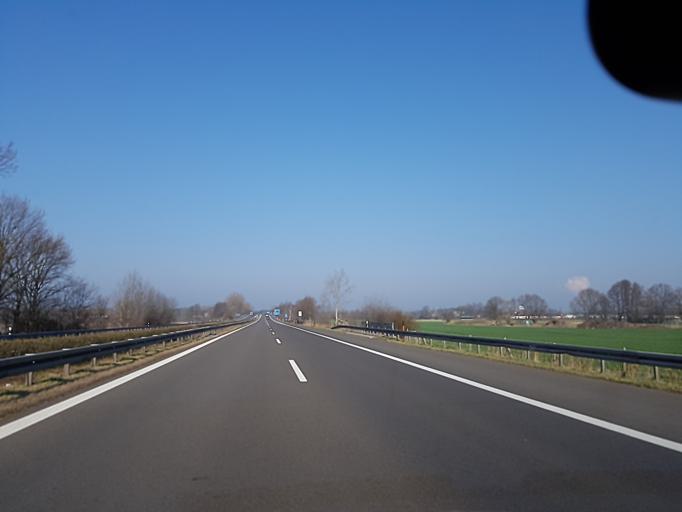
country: DE
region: Brandenburg
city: Forst
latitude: 51.7084
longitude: 14.6259
